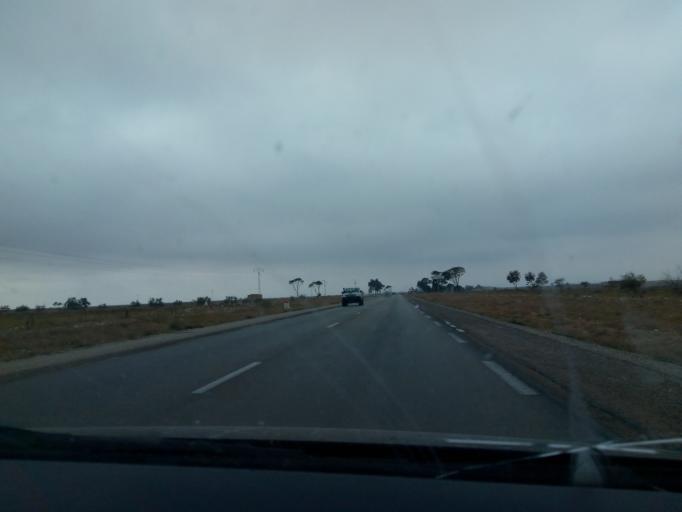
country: TN
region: Madanin
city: Medenine
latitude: 33.2751
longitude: 10.4686
